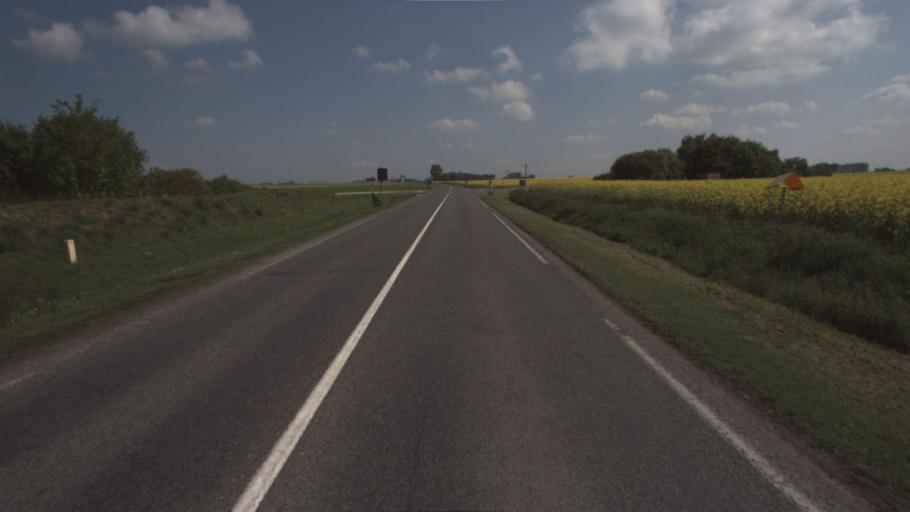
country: FR
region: Ile-de-France
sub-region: Departement de Seine-et-Marne
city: Moisenay
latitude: 48.5912
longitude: 2.7250
